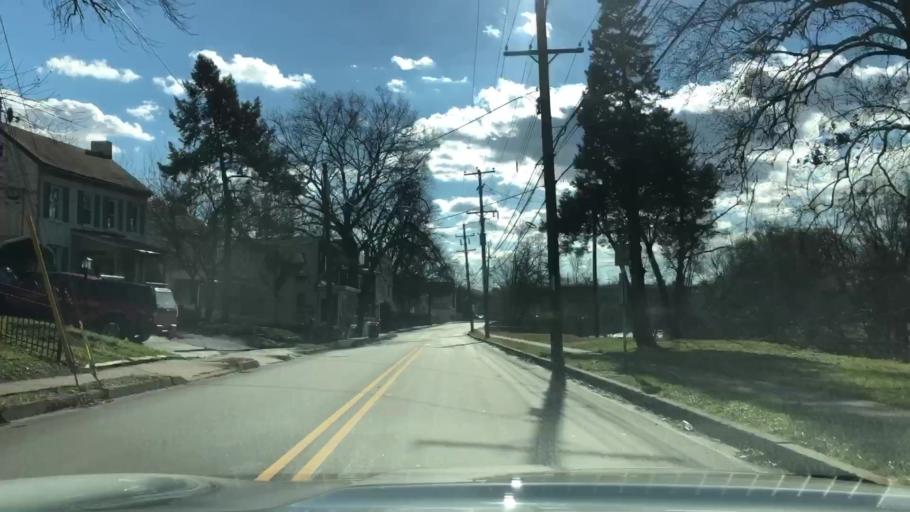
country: US
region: Pennsylvania
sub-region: Montgomery County
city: Pottstown
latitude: 40.2501
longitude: -75.6547
